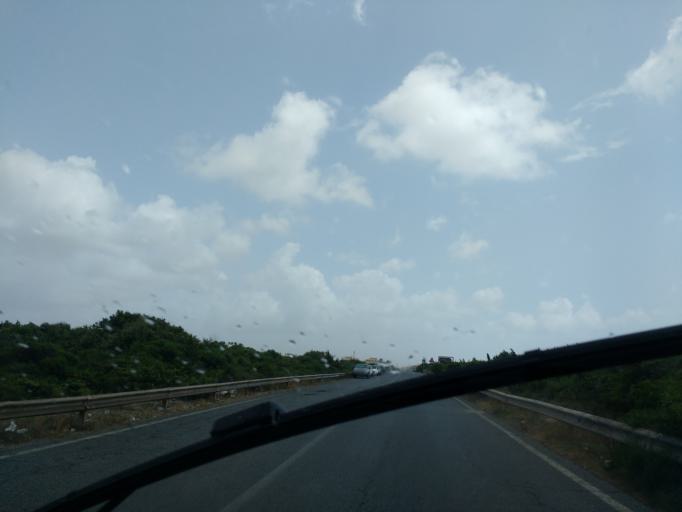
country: IT
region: Latium
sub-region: Citta metropolitana di Roma Capitale
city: Torvaianica
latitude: 41.6520
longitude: 12.4233
